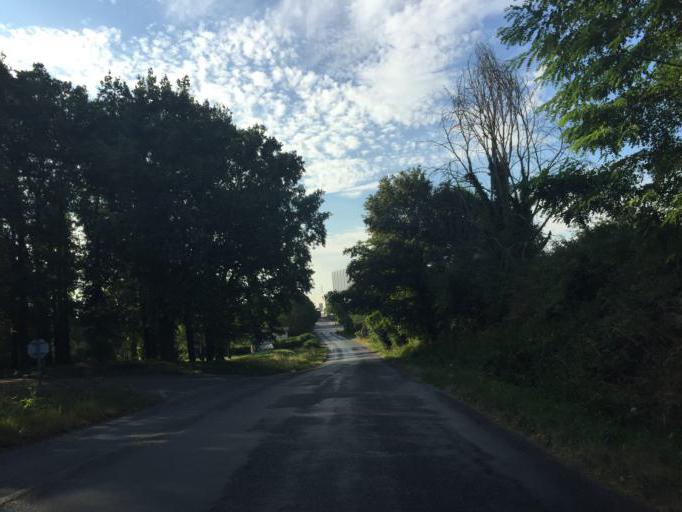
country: FR
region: Auvergne
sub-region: Departement de l'Allier
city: Toulon-sur-Allier
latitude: 46.5393
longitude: 3.3573
